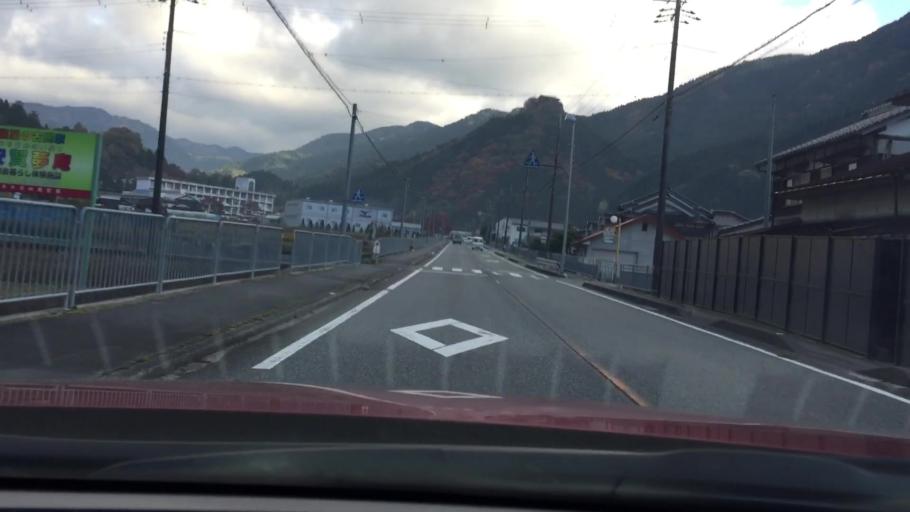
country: JP
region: Hyogo
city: Yamazakicho-nakabirose
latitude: 35.1504
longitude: 134.5412
